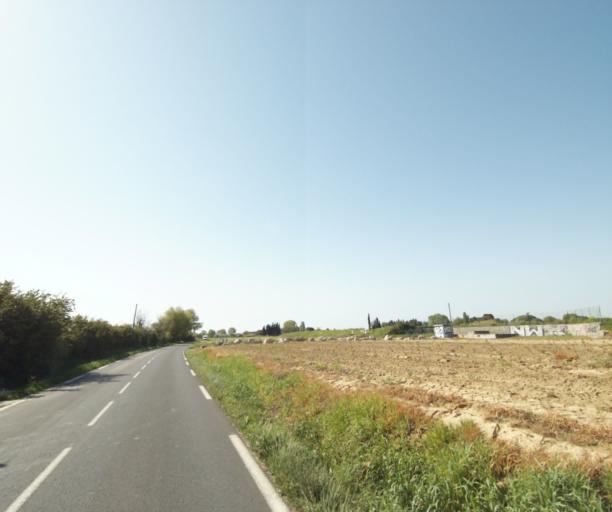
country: FR
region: Languedoc-Roussillon
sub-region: Departement de l'Herault
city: Lattes
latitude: 43.5849
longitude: 3.9086
